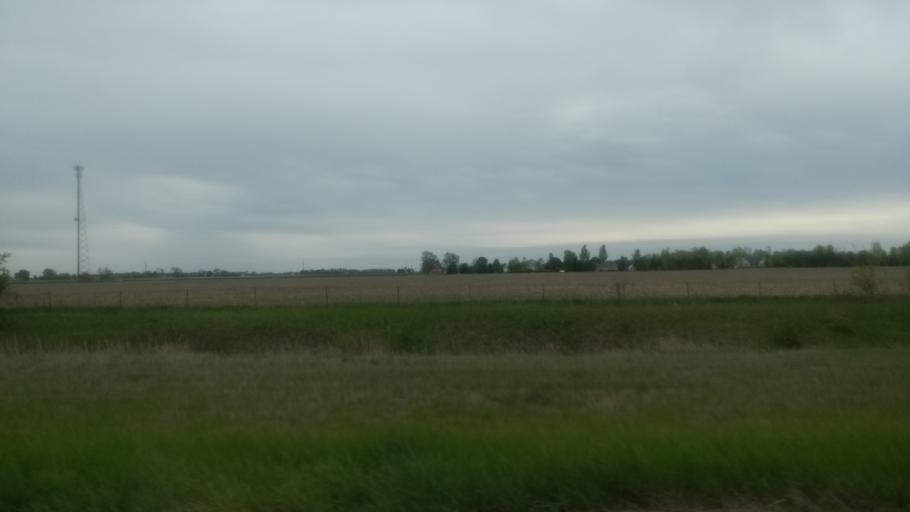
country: US
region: Ohio
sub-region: Wood County
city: Bowling Green
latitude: 41.3521
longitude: -83.6063
